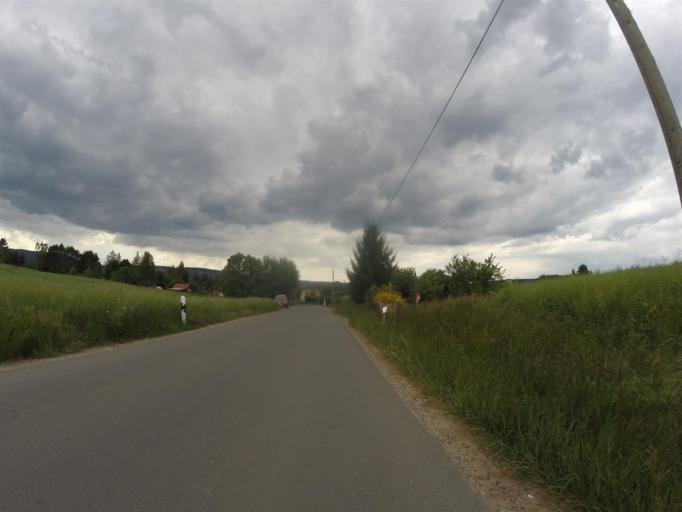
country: DE
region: Thuringia
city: Zollnitz
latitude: 50.8645
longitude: 11.6251
